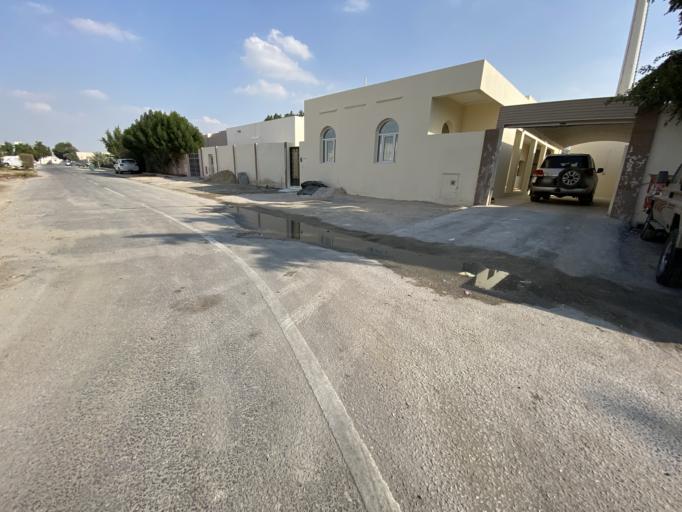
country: QA
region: Baladiyat ar Rayyan
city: Ar Rayyan
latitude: 25.2310
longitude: 51.3766
